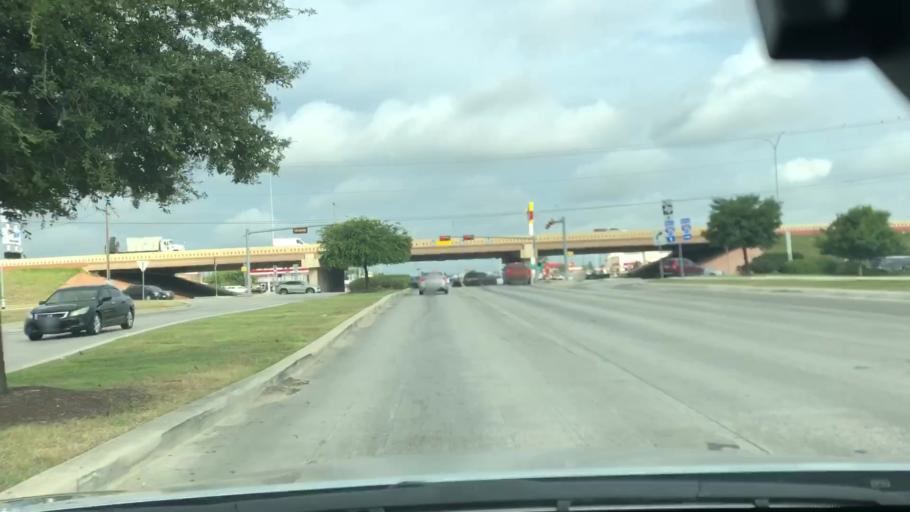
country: US
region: Texas
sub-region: Guadalupe County
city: Lake Dunlap
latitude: 29.7282
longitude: -98.0774
